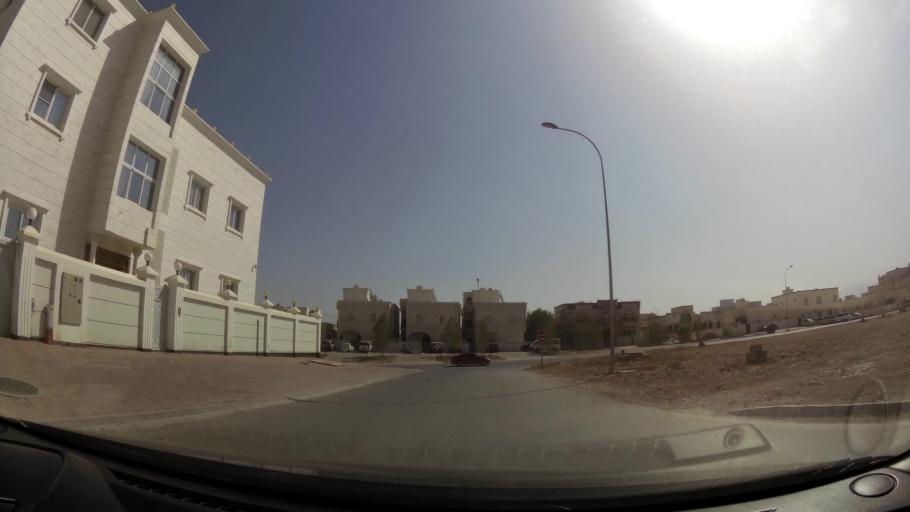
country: OM
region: Zufar
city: Salalah
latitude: 17.0028
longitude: 54.0171
